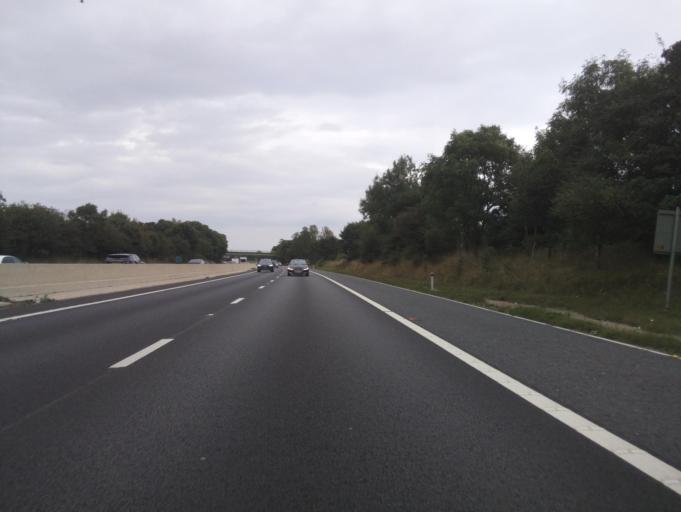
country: GB
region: England
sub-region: Darlington
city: Coatham Mundeville
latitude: 54.5958
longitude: -1.5426
